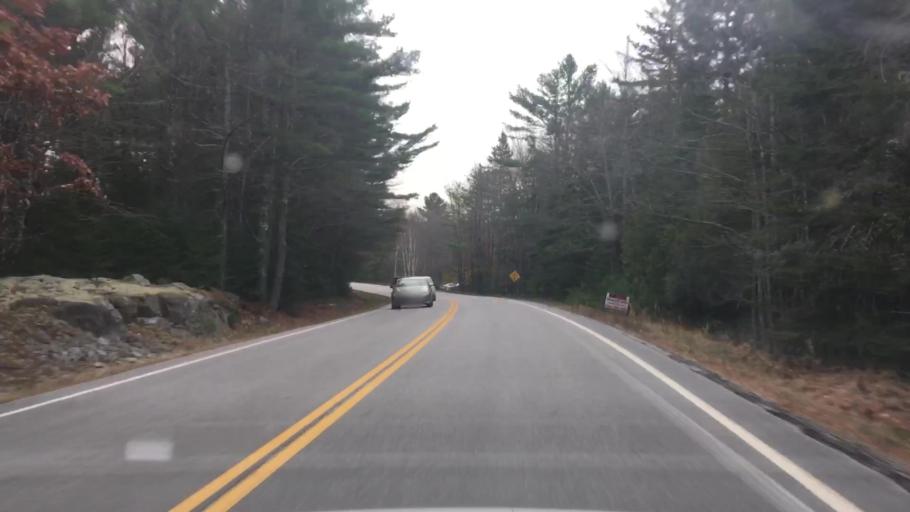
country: US
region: Maine
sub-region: Hancock County
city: Penobscot
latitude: 44.5061
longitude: -68.6557
